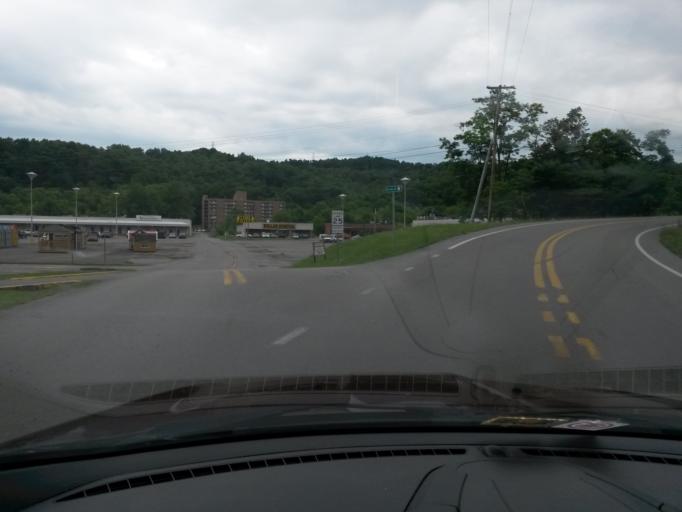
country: US
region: West Virginia
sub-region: Lewis County
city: Weston
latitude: 39.0365
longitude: -80.4473
